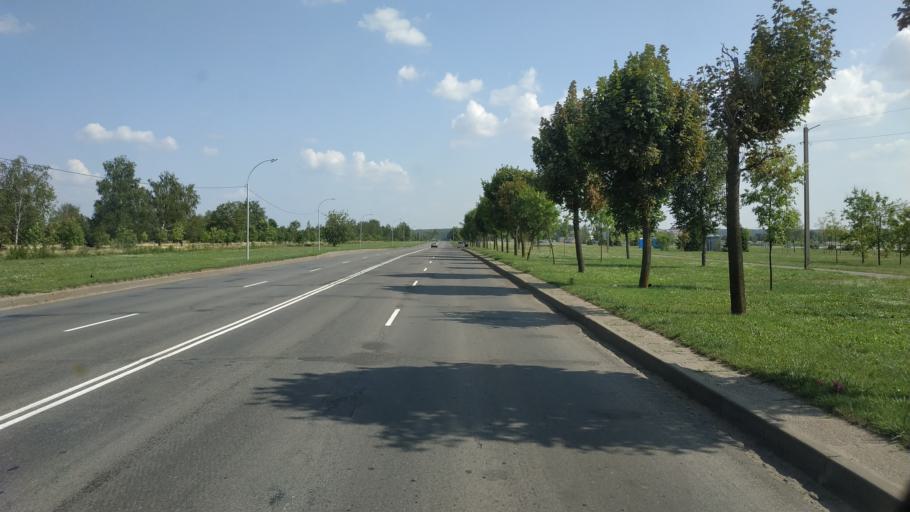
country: BY
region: Mogilev
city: Buynichy
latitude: 53.8631
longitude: 30.3204
